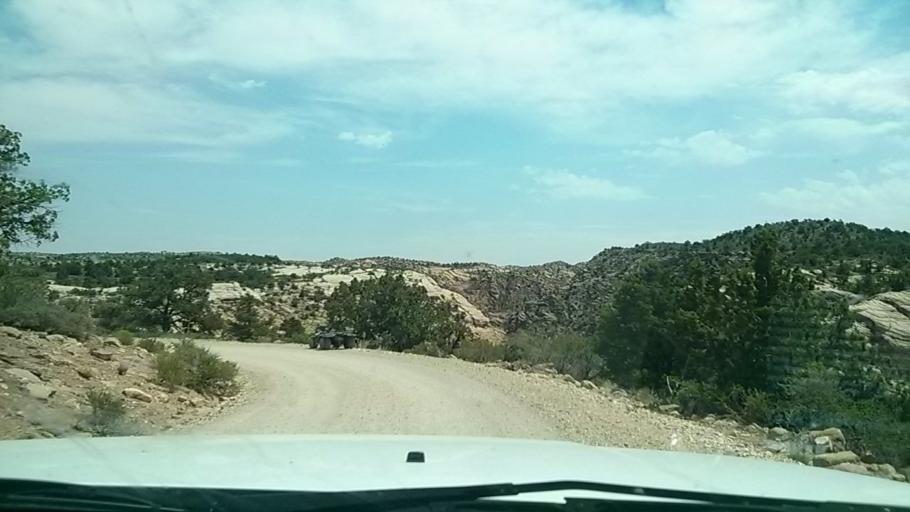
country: US
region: Utah
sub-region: Washington County
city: Washington
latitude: 37.2372
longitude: -113.4490
